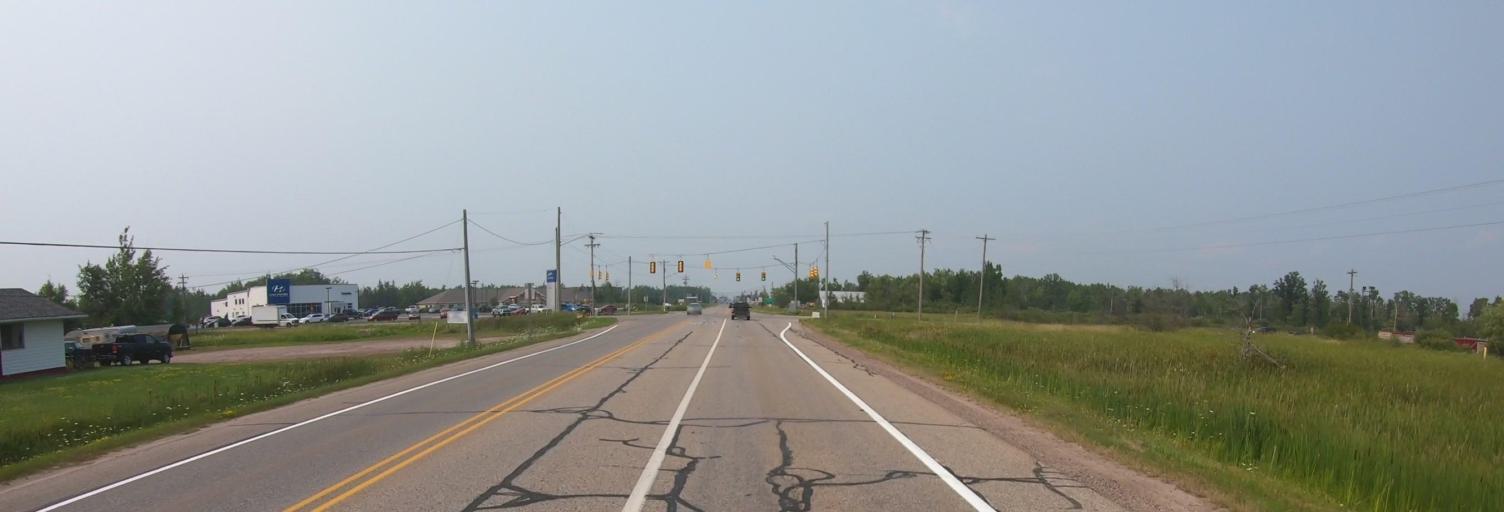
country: US
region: Michigan
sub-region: Chippewa County
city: Sault Ste. Marie
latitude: 46.4621
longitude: -84.3539
